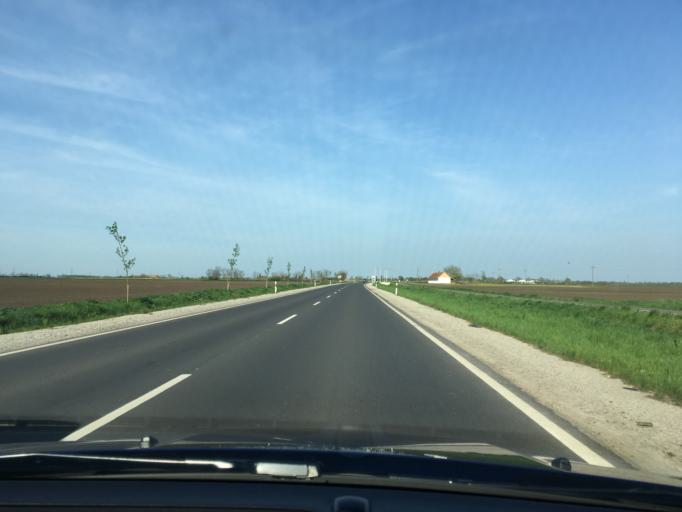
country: HU
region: Bekes
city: Csorvas
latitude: 46.6476
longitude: 20.9011
